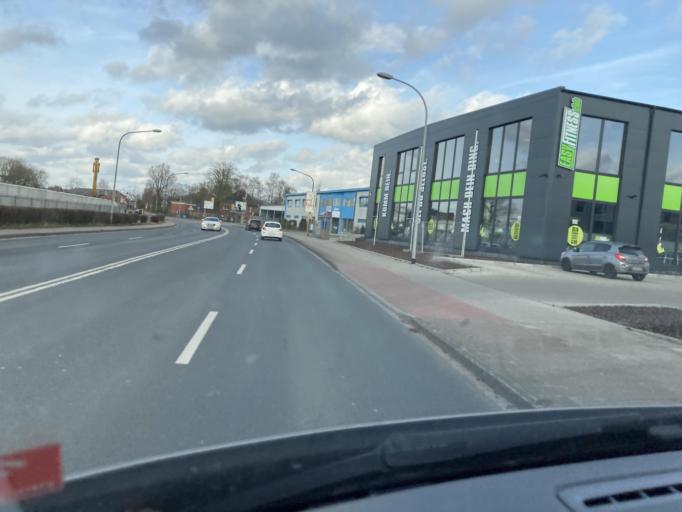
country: DE
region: Lower Saxony
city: Leer
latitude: 53.2248
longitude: 7.4633
